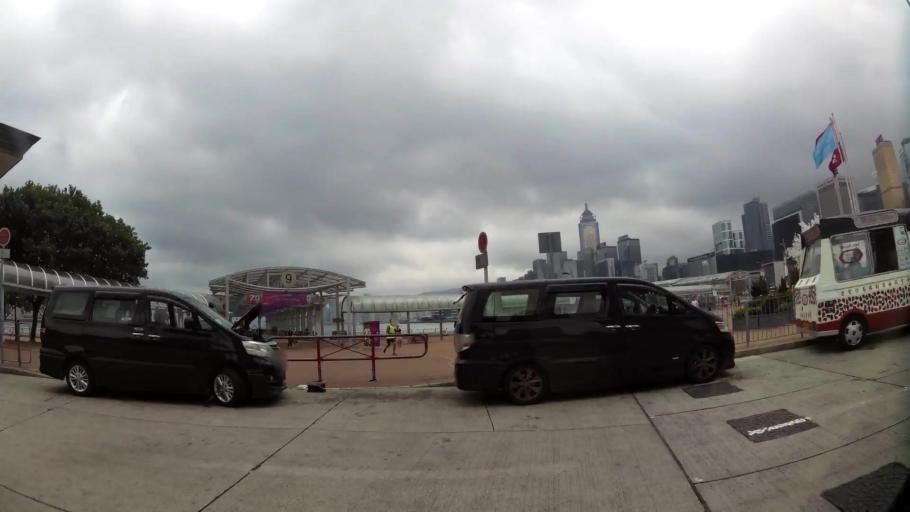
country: HK
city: Hong Kong
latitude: 22.2859
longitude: 114.1618
